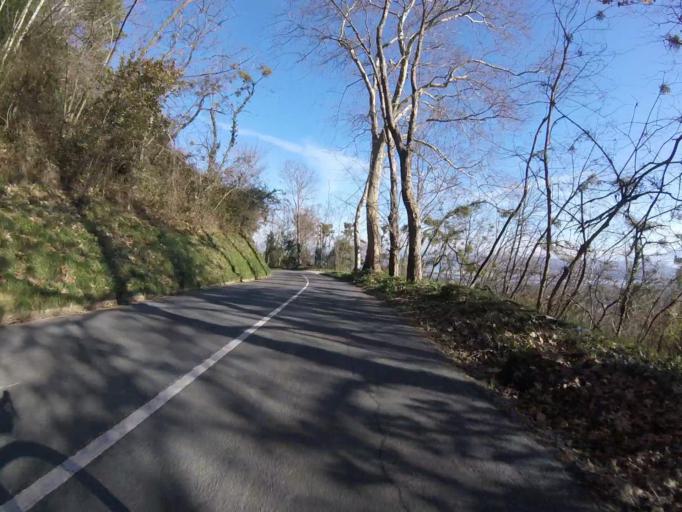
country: ES
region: Basque Country
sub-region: Provincia de Guipuzcoa
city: Fuenterrabia
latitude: 43.3697
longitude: -1.8111
